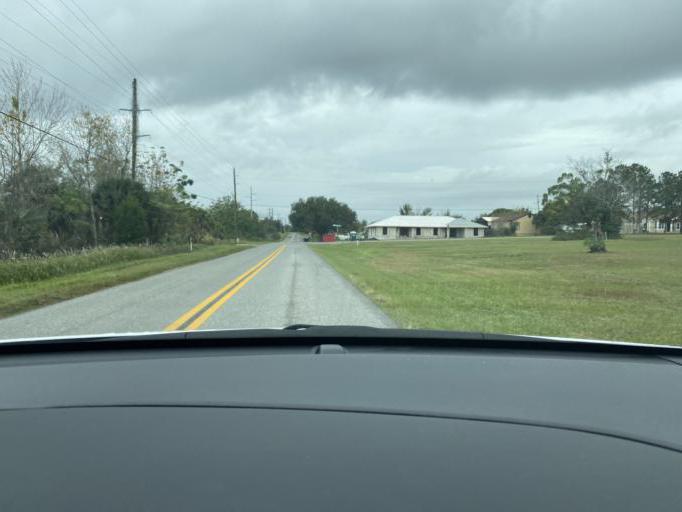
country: US
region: Florida
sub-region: Lake County
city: Minneola
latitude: 28.5947
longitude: -81.7802
